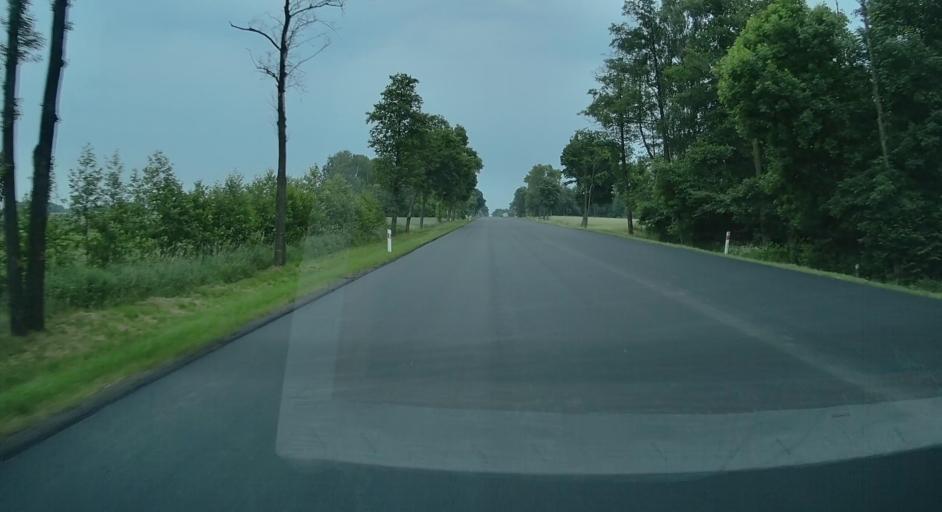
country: PL
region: Lublin Voivodeship
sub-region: Powiat lukowski
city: Trzebieszow
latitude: 52.0550
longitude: 22.6419
